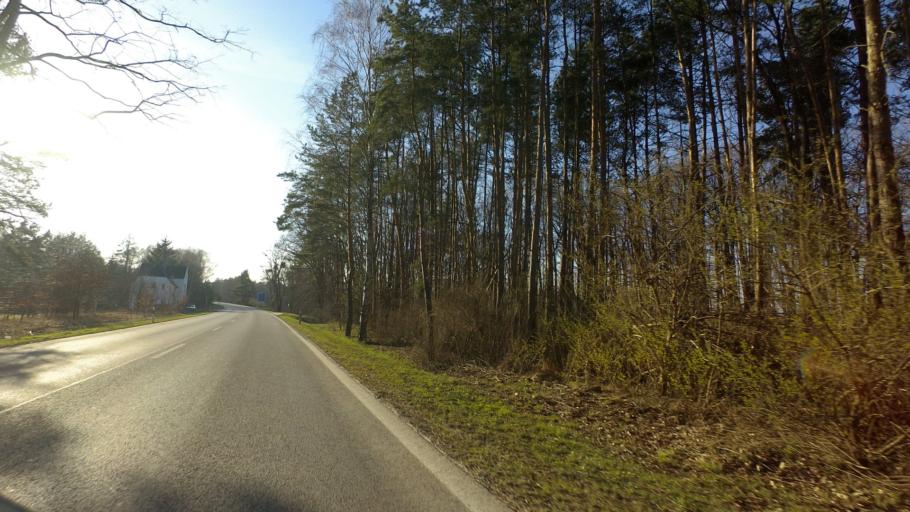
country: DE
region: Brandenburg
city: Althuttendorf
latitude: 52.9518
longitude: 13.8150
